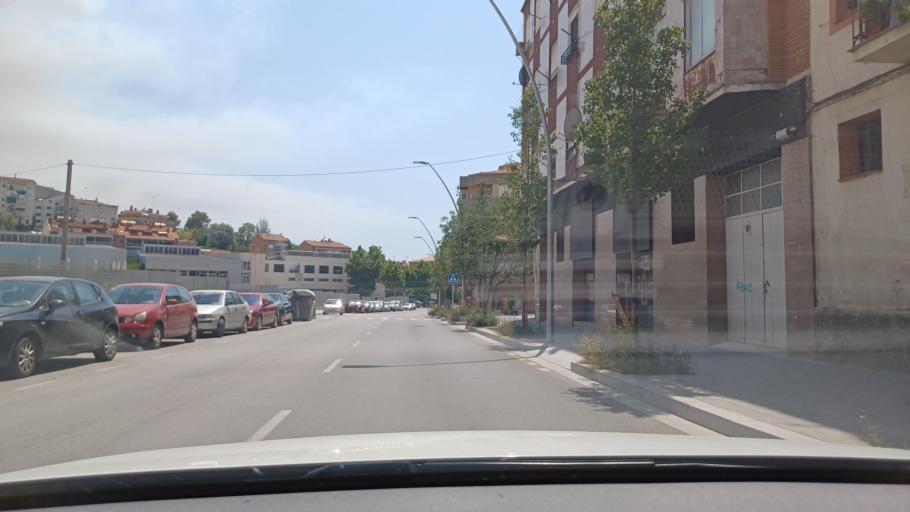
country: ES
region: Catalonia
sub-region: Provincia de Barcelona
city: Manresa
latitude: 41.7267
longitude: 1.8318
